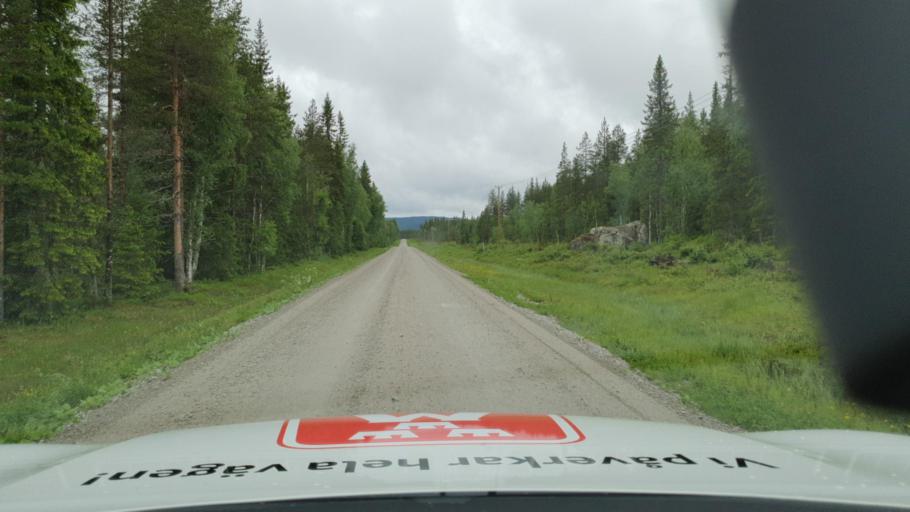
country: SE
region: Vaesterbotten
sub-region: Dorotea Kommun
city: Dorotea
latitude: 63.9811
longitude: 16.8264
